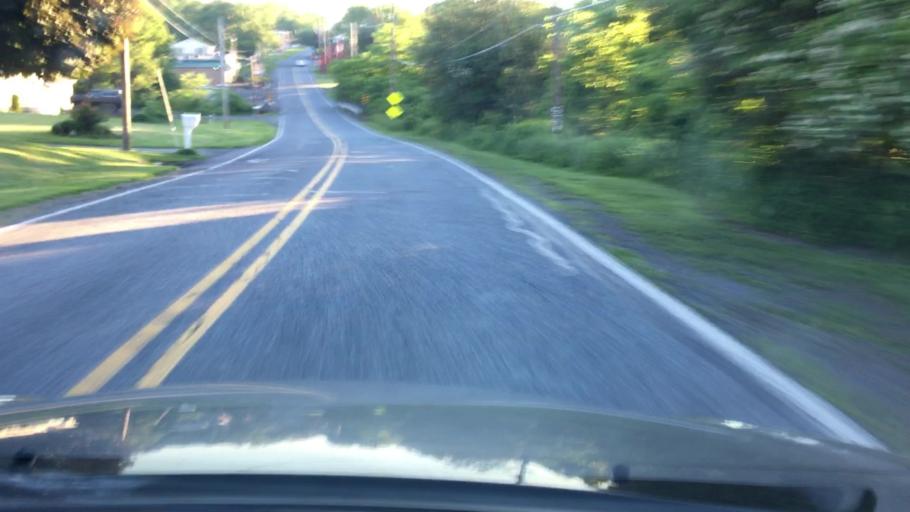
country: US
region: Pennsylvania
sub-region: Luzerne County
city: Harleigh
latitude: 41.0178
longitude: -75.9957
